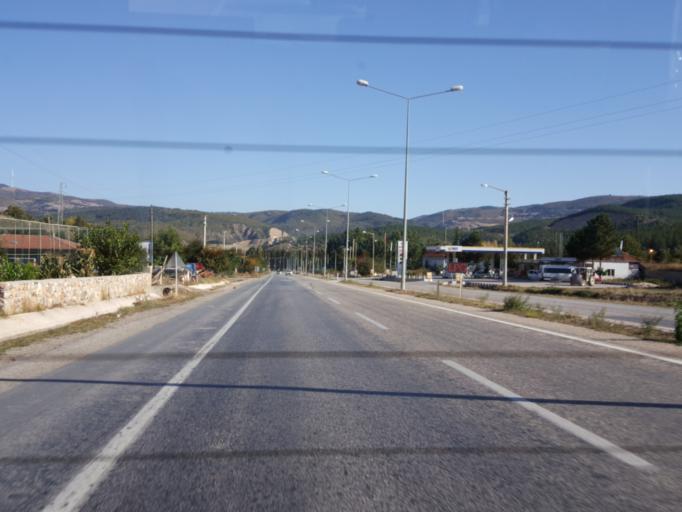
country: TR
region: Amasya
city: Ezinepazari
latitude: 40.5622
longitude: 36.1393
